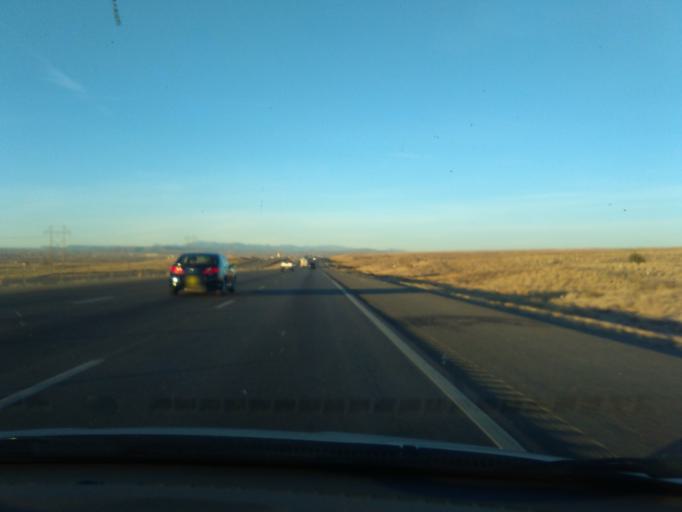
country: US
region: New Mexico
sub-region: Sandoval County
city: Corrales
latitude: 35.2269
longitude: -106.5716
